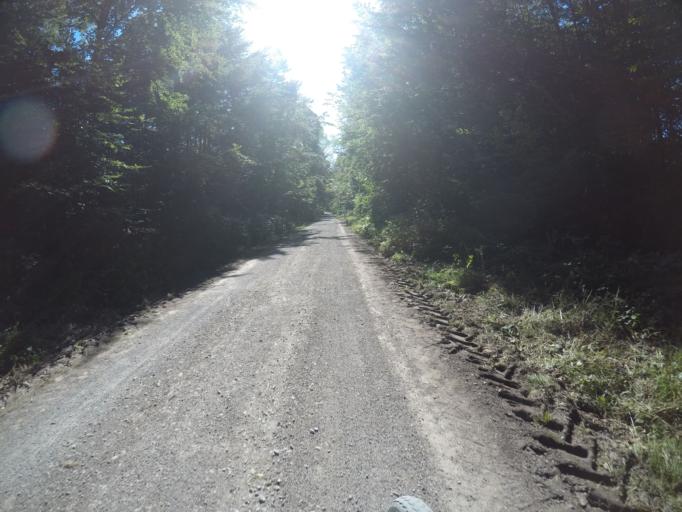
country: DE
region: Baden-Wuerttemberg
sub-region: Regierungsbezirk Stuttgart
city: Gerlingen
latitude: 48.7712
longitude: 9.1084
